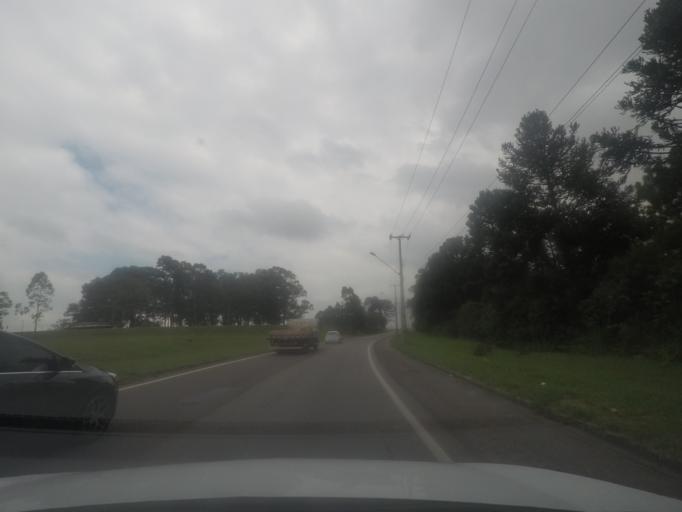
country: BR
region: Parana
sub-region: Sao Jose Dos Pinhais
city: Sao Jose dos Pinhais
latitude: -25.5416
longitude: -49.3034
